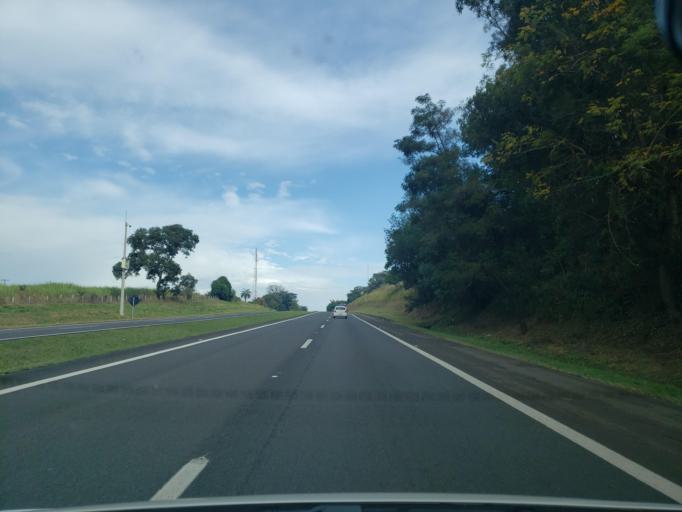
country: BR
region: Sao Paulo
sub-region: Itirapina
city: Itirapina
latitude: -22.2755
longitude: -47.9702
